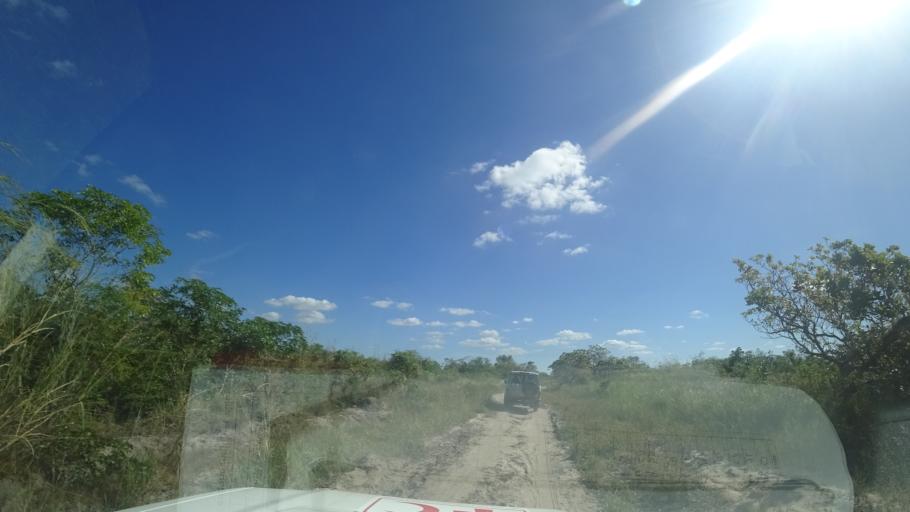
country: MZ
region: Sofala
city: Dondo
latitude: -19.4815
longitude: 34.6229
